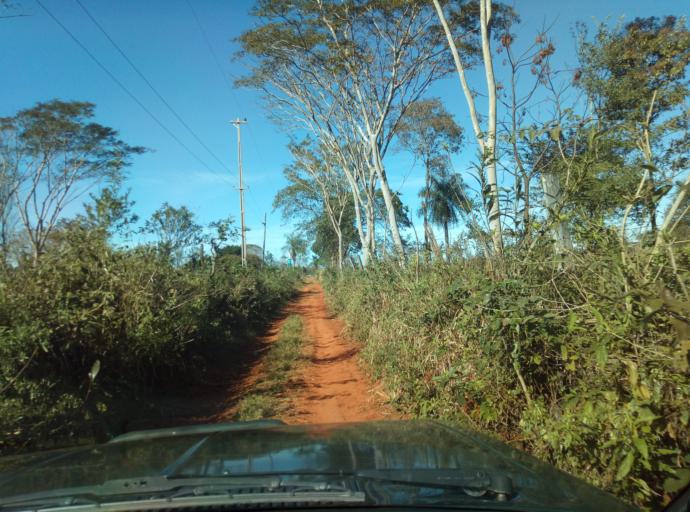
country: PY
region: Caaguazu
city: Doctor Cecilio Baez
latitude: -25.1817
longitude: -56.2423
